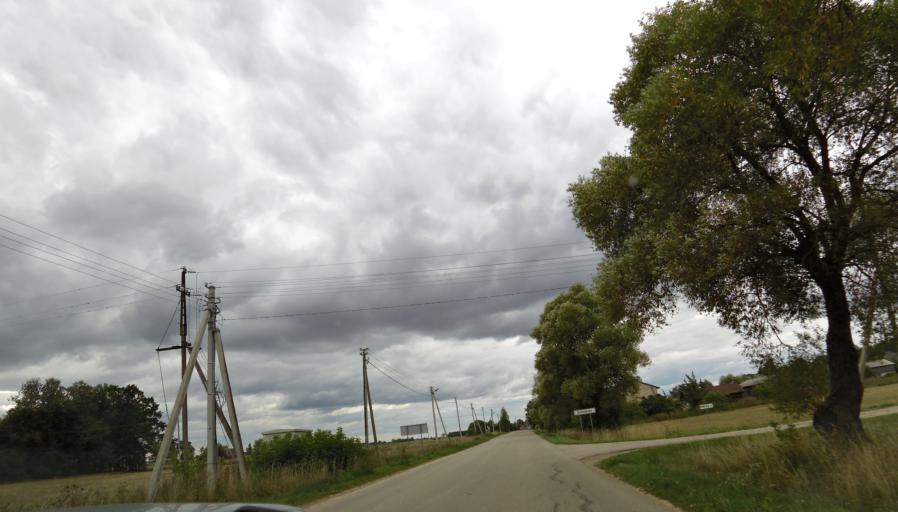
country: LT
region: Panevezys
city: Pasvalys
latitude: 56.0743
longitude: 24.2960
